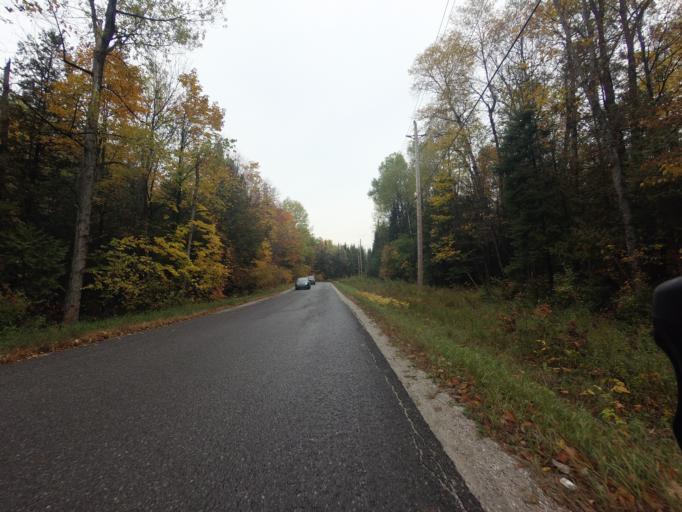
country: CA
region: Ontario
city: Perth
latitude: 45.1155
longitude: -76.5080
